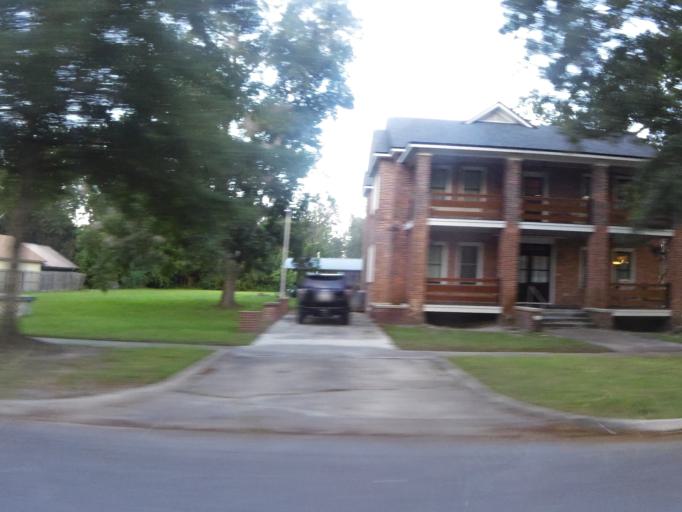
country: US
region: Georgia
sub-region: Camden County
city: St. Marys
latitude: 30.7307
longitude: -81.5462
